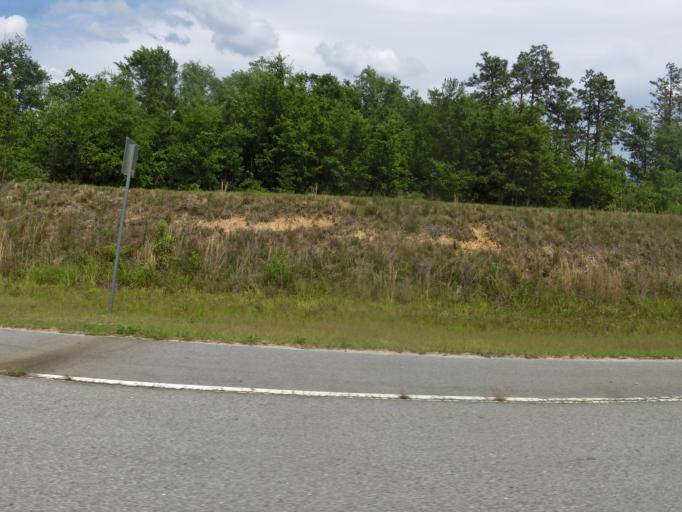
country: US
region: Georgia
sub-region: Emanuel County
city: Swainsboro
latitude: 32.6721
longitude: -82.3849
